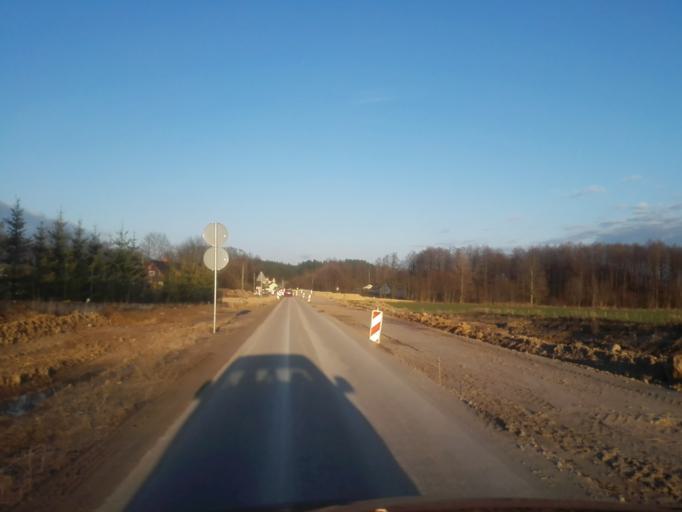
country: PL
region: Podlasie
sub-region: Powiat sejnenski
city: Krasnopol
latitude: 54.0827
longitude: 23.0867
